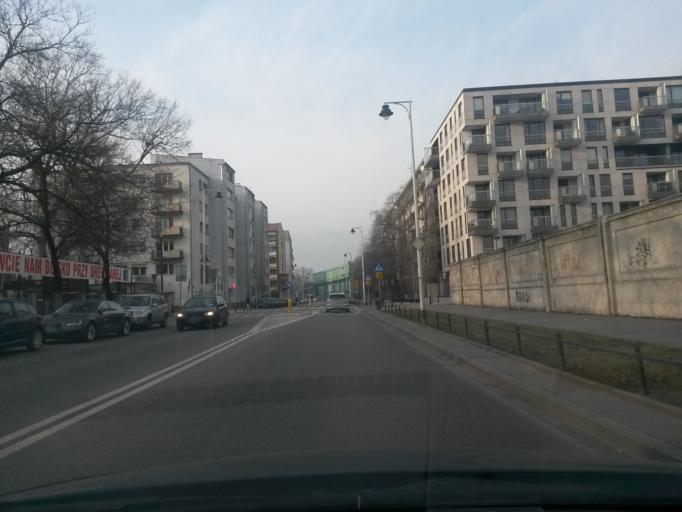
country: PL
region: Masovian Voivodeship
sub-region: Warszawa
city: Srodmiescie
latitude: 52.2404
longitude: 21.0262
